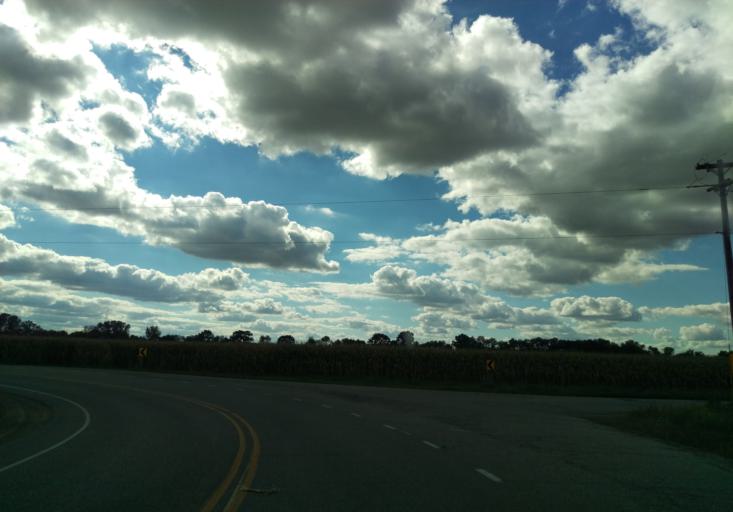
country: US
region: Wisconsin
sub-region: Dane County
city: Stoughton
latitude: 42.8749
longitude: -89.2400
